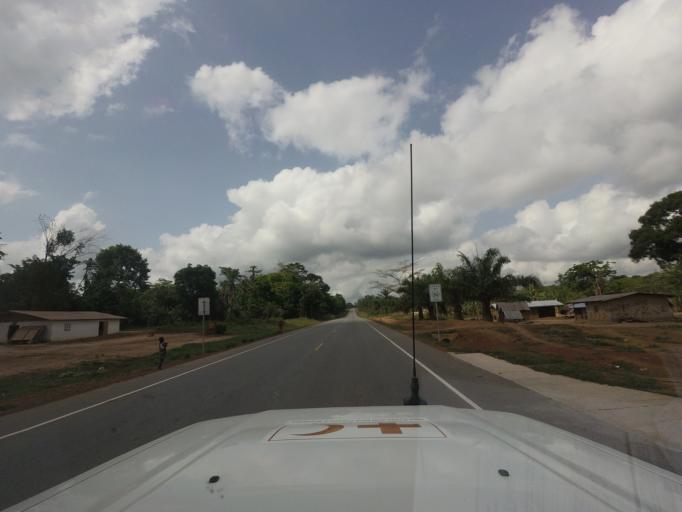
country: LR
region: Nimba
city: Sanniquellie
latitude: 7.1489
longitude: -9.0536
